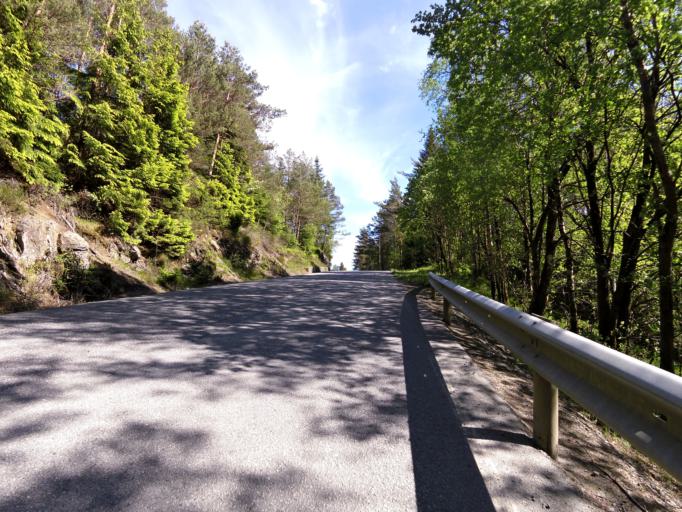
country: NO
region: Hordaland
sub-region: Stord
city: Leirvik
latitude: 59.7868
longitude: 5.4493
